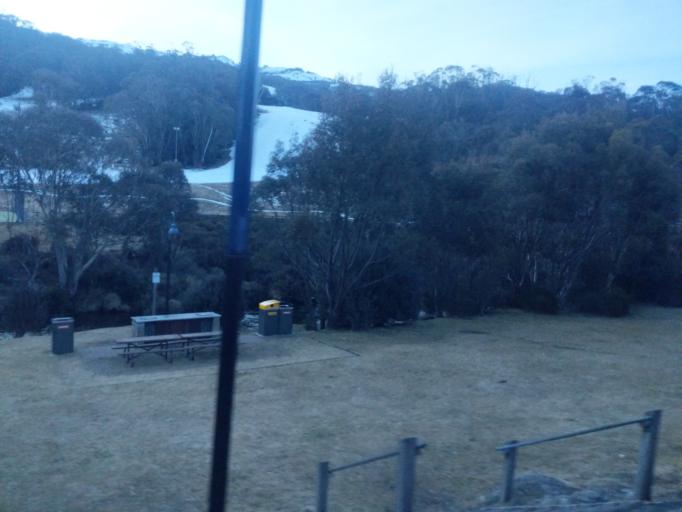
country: AU
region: New South Wales
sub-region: Snowy River
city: Jindabyne
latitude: -36.5038
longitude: 148.3055
